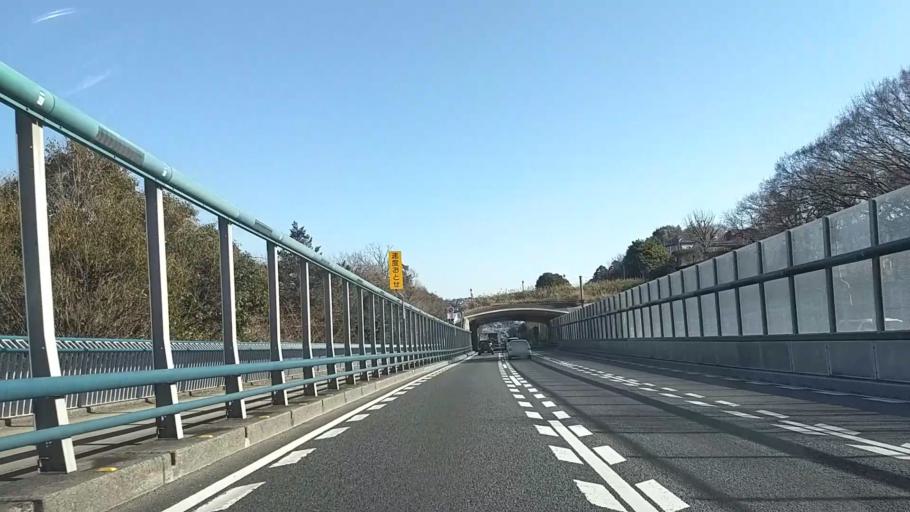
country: JP
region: Kanagawa
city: Yokohama
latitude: 35.4681
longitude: 139.5665
